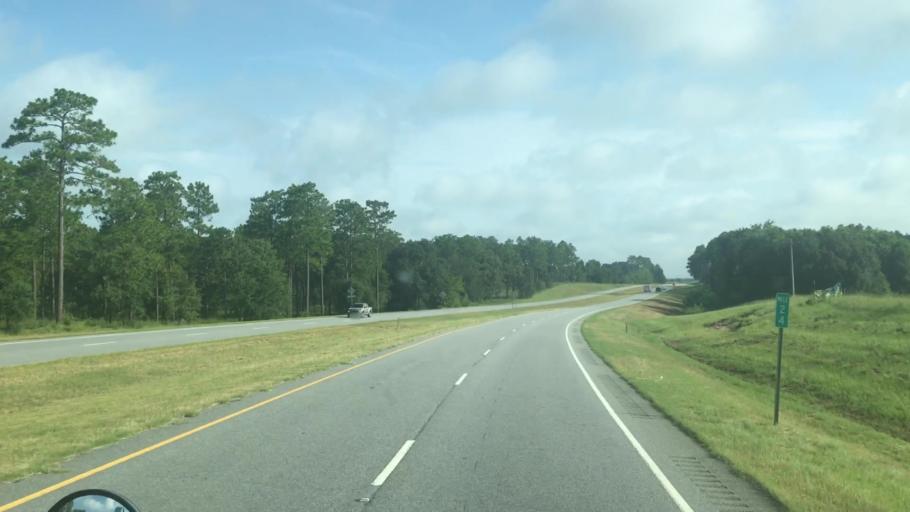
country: US
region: Georgia
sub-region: Decatur County
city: Bainbridge
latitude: 30.9481
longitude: -84.6120
